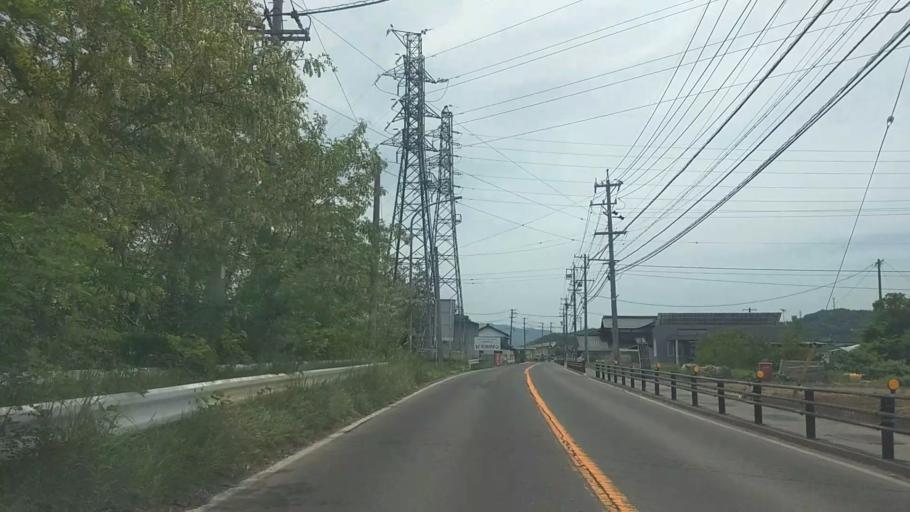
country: JP
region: Nagano
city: Saku
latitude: 36.1868
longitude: 138.4812
